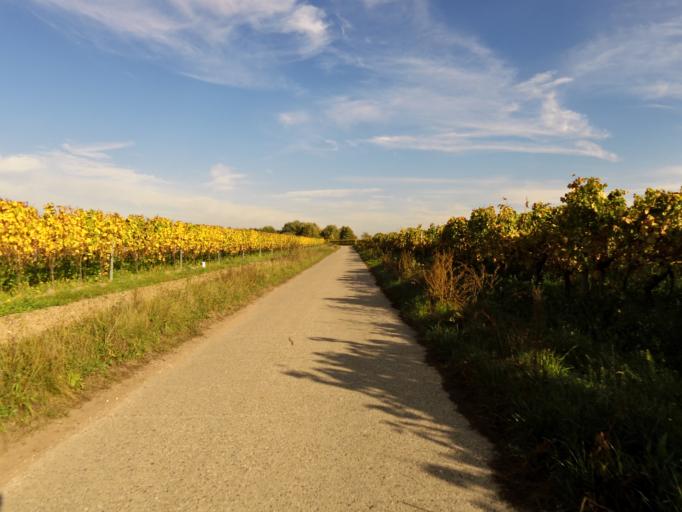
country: DE
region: Rheinland-Pfalz
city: Niederkirchen bei Deidesheim
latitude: 49.4295
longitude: 8.2070
